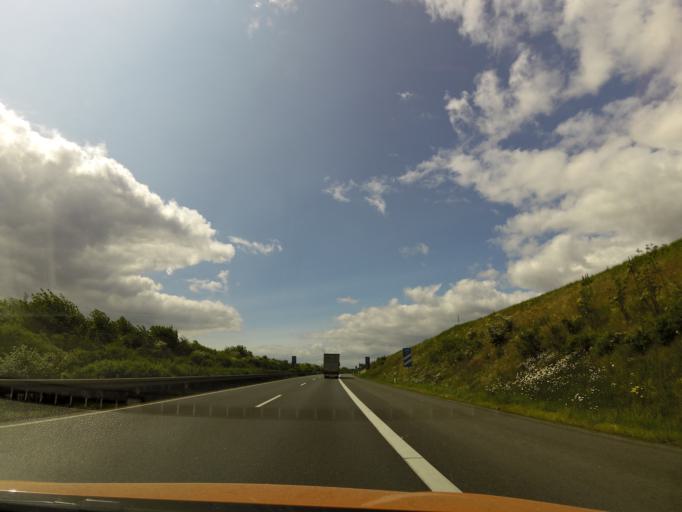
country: DE
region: Lower Saxony
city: Leiferde
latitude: 52.1995
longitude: 10.4681
